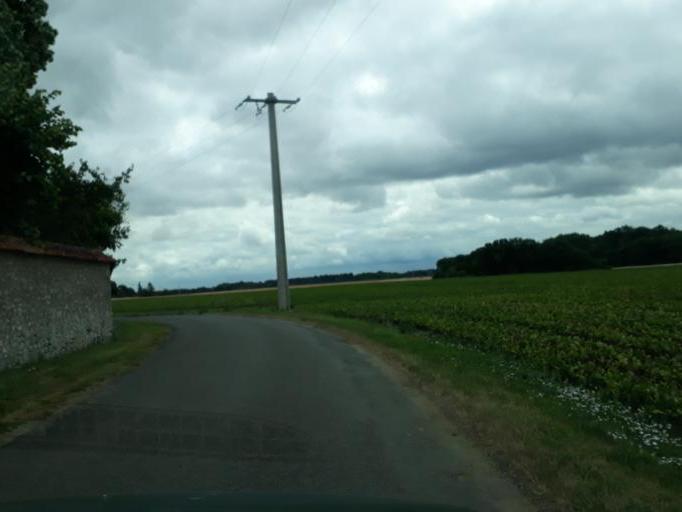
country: FR
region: Centre
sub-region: Departement du Loiret
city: Saint-Cyr-en-Val
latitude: 47.8449
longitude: 1.9876
